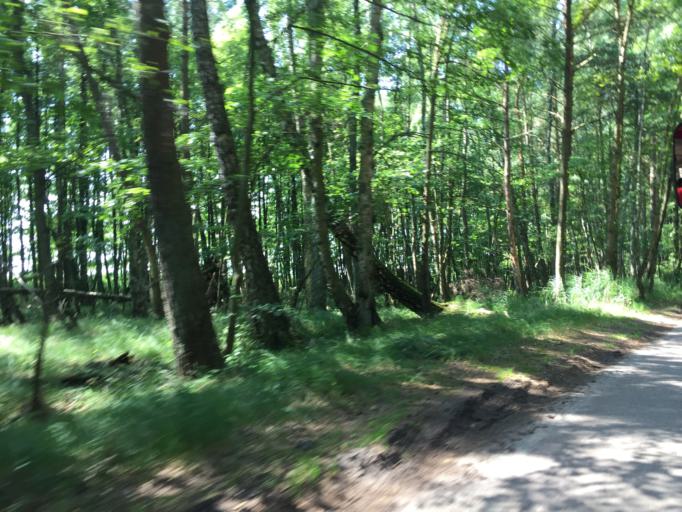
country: PL
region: Pomeranian Voivodeship
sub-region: Powiat leborski
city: Leba
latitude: 54.7524
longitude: 17.4864
